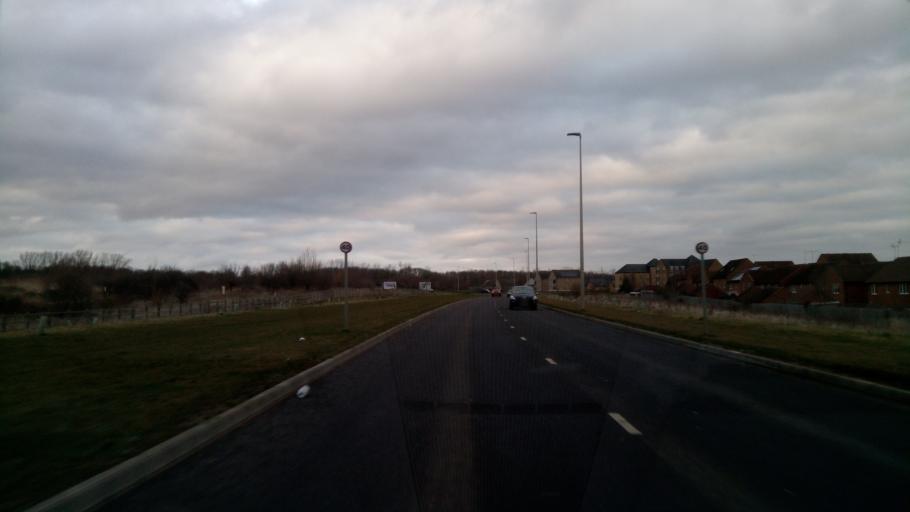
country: GB
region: England
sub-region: Cambridgeshire
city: Yaxley
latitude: 52.5360
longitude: -0.2826
